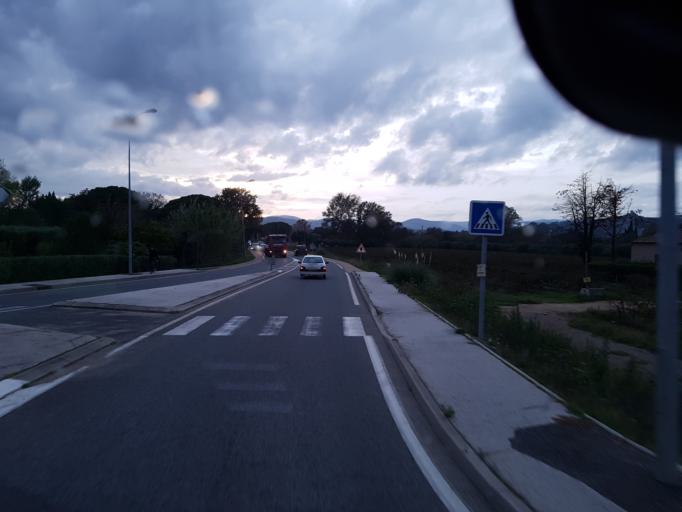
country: FR
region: Provence-Alpes-Cote d'Azur
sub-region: Departement du Var
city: Grimaud
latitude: 43.2701
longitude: 6.5502
